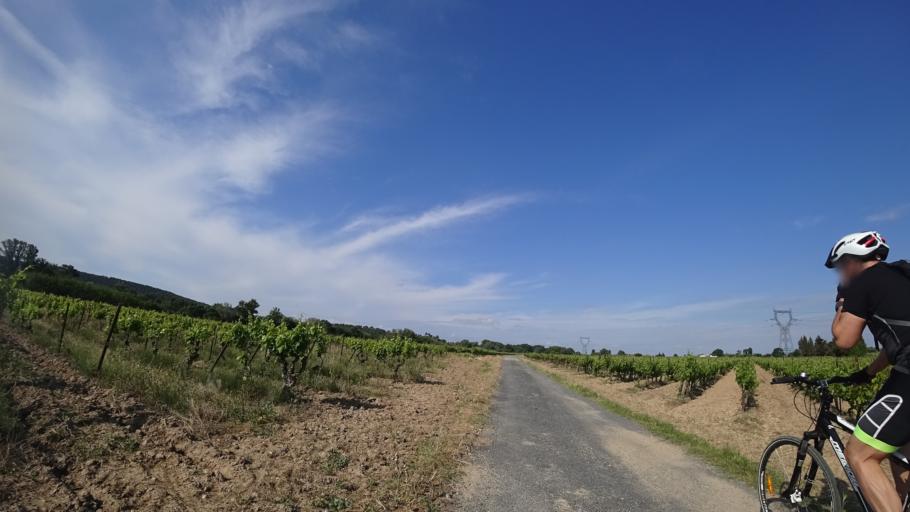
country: FR
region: Languedoc-Roussillon
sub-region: Departement de l'Herault
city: Olonzac
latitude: 43.2631
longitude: 2.7316
